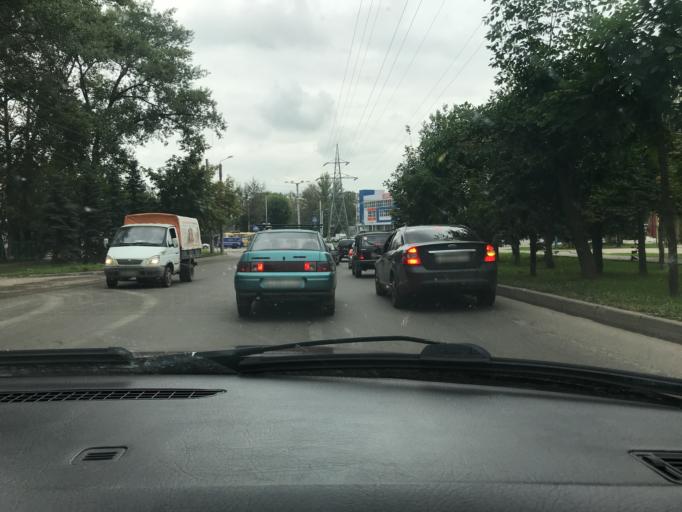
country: RU
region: Kaluga
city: Kaluga
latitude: 54.5240
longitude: 36.2933
